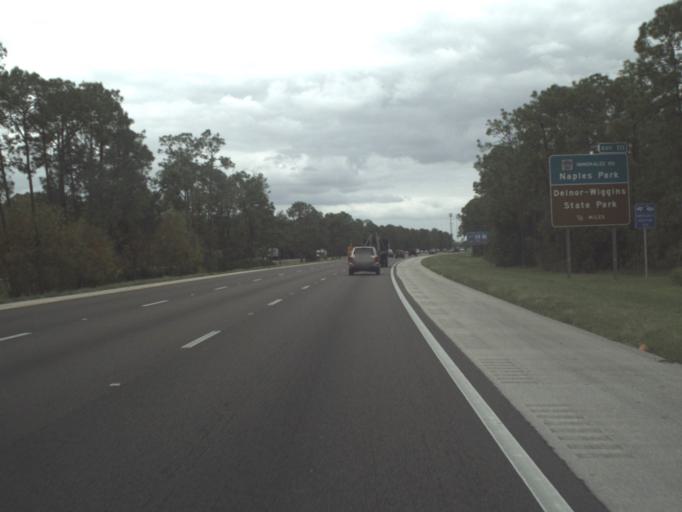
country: US
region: Florida
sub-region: Collier County
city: Vineyards
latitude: 26.2603
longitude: -81.7418
